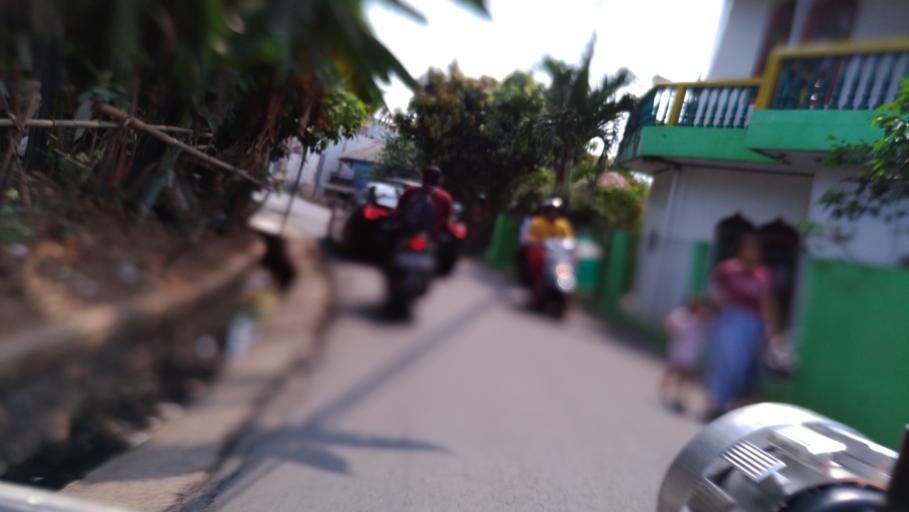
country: ID
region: West Java
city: Depok
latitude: -6.3541
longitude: 106.8738
